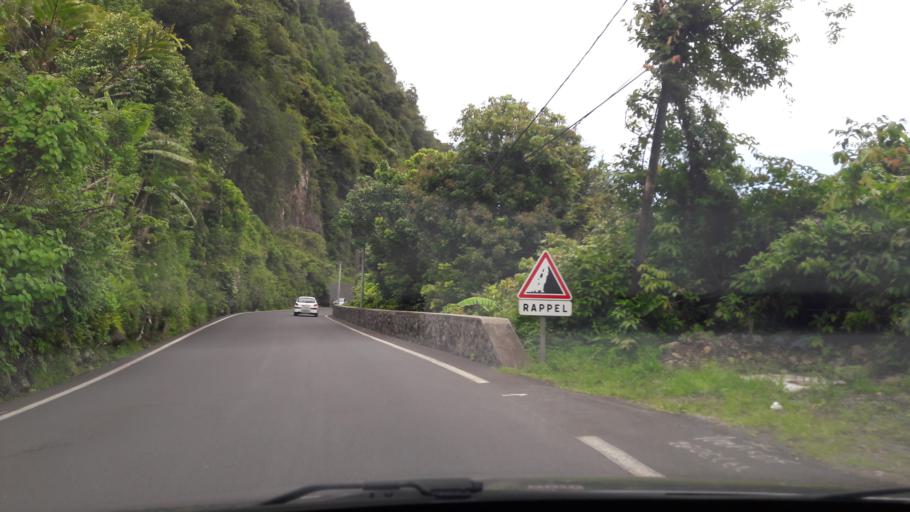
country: RE
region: Reunion
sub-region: Reunion
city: Saint-Andre
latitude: -20.9875
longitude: 55.6201
